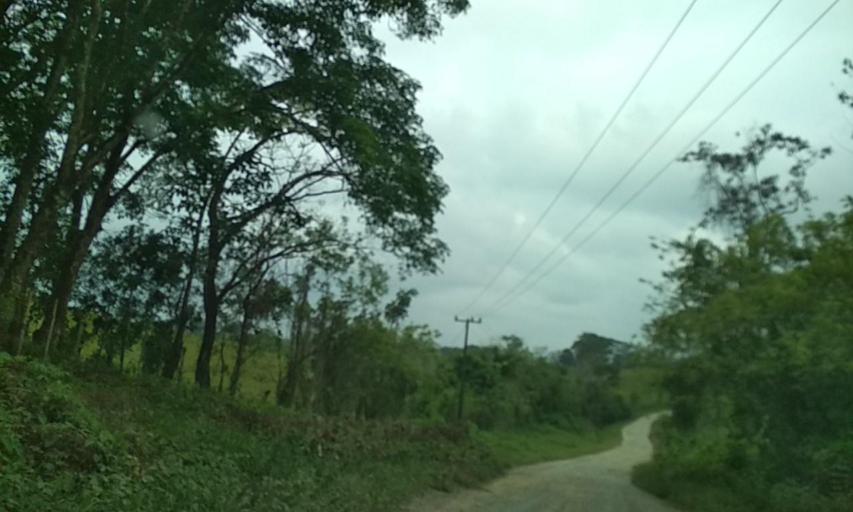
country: MX
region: Veracruz
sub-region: Uxpanapa
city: Poblado 10
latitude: 17.4898
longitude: -94.1297
